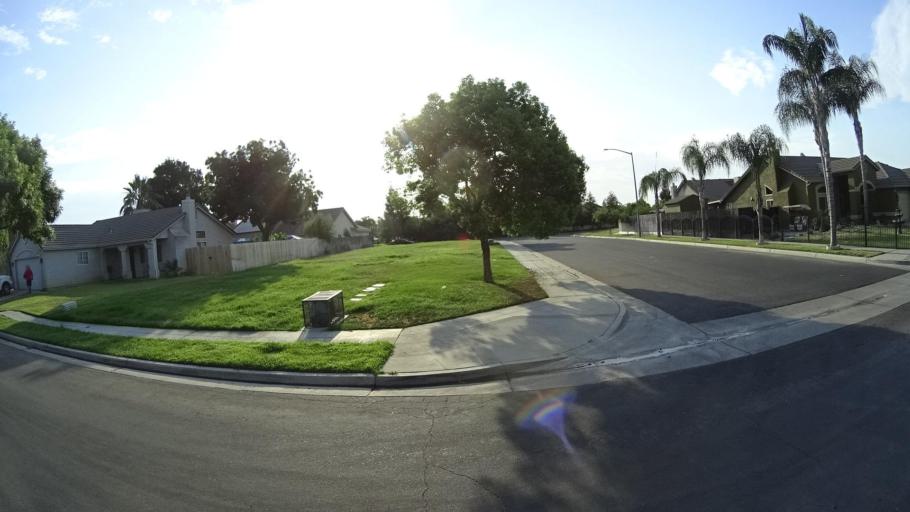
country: US
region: California
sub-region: Fresno County
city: Sunnyside
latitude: 36.7105
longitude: -119.7073
